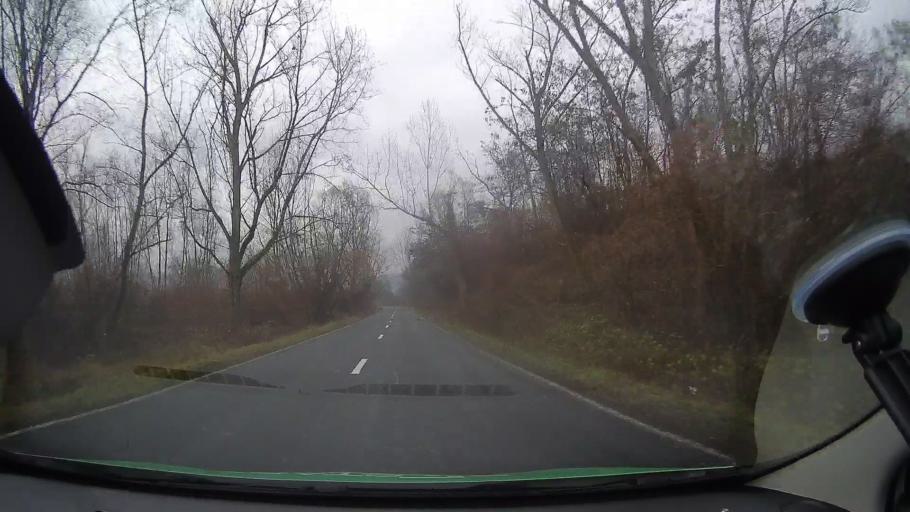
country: RO
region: Arad
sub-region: Comuna Plescuta
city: Plescuta
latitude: 46.2921
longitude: 22.4044
